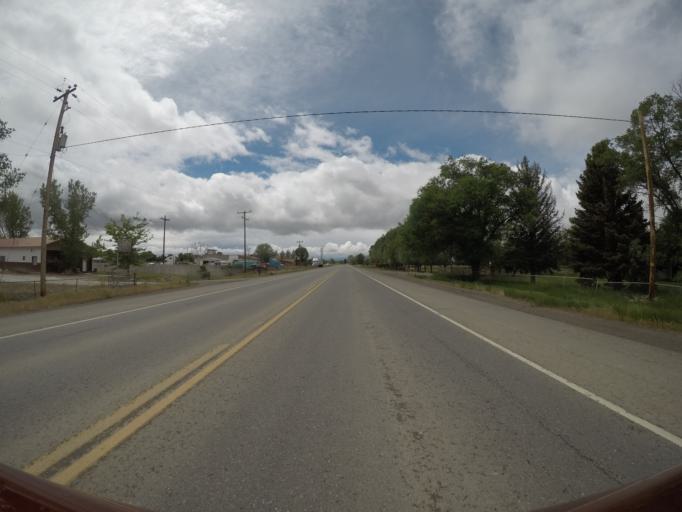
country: US
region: Wyoming
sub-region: Big Horn County
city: Lovell
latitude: 44.8405
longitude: -108.3702
